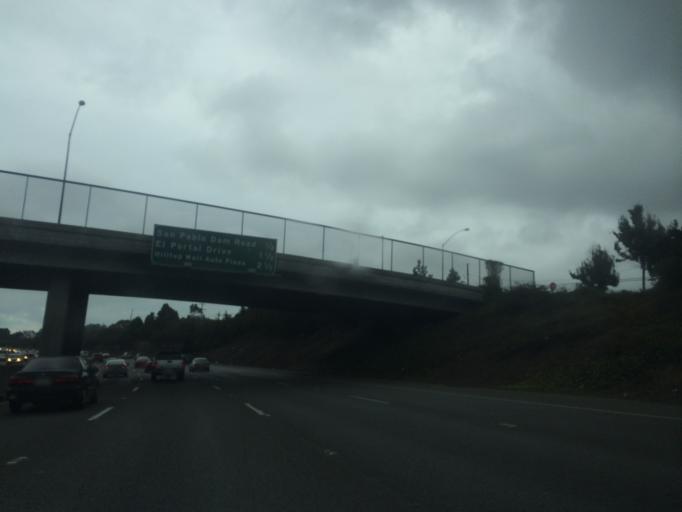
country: US
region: California
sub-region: Contra Costa County
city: East Richmond Heights
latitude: 37.9429
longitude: -122.3237
